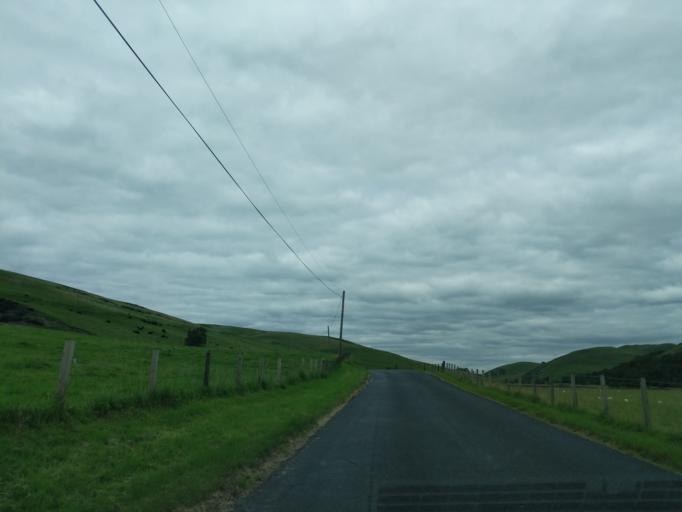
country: GB
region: Scotland
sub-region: The Scottish Borders
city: West Linton
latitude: 55.6776
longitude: -3.3309
